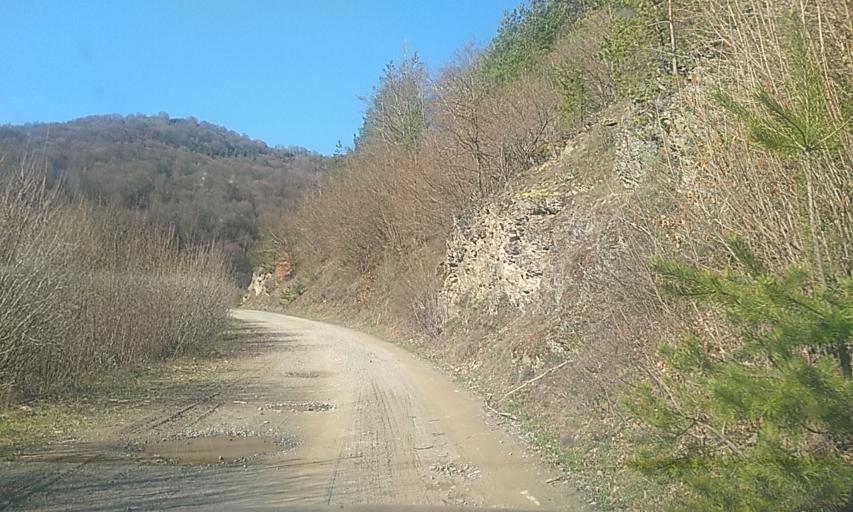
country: MK
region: Kriva Palanka
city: Kriva Palanka
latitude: 42.3427
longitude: 22.3924
